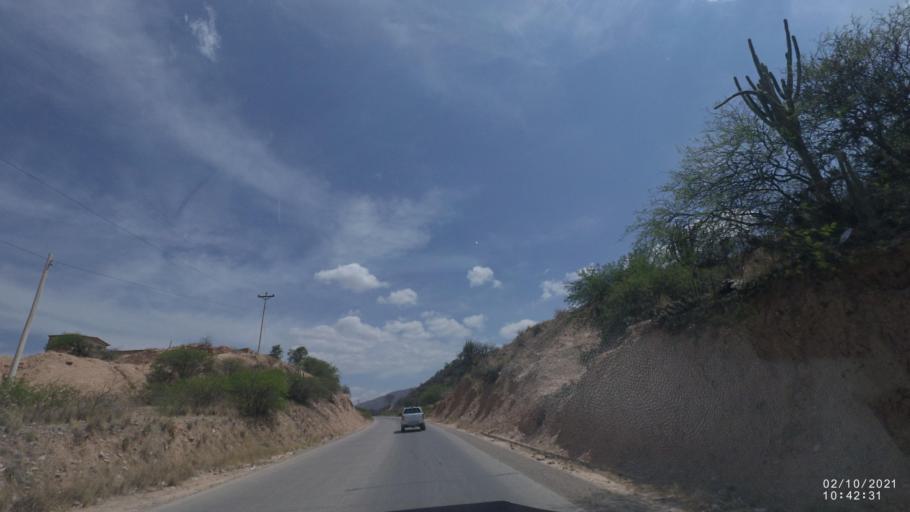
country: BO
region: Cochabamba
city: Capinota
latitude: -17.6065
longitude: -66.2949
